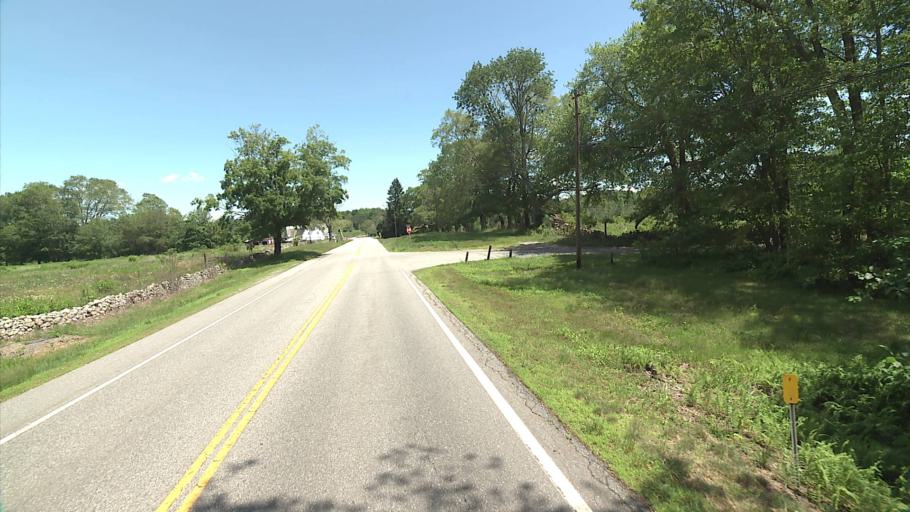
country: US
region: Connecticut
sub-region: New London County
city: Old Mystic
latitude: 41.4280
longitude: -71.9284
